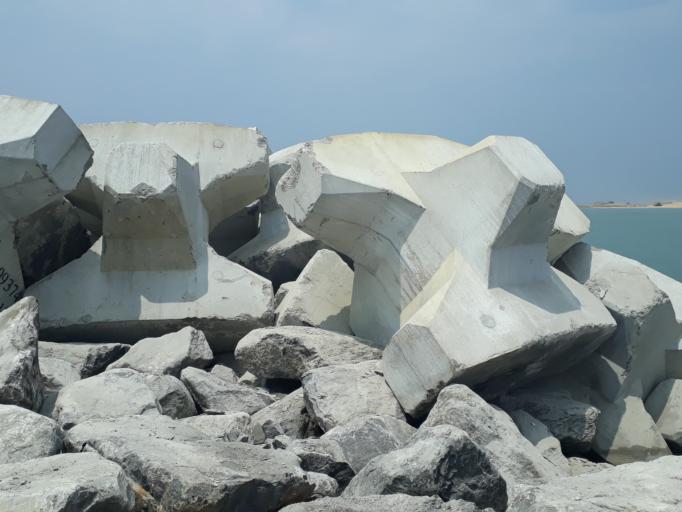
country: LK
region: Western
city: Colombo
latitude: 6.9233
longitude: 79.8273
